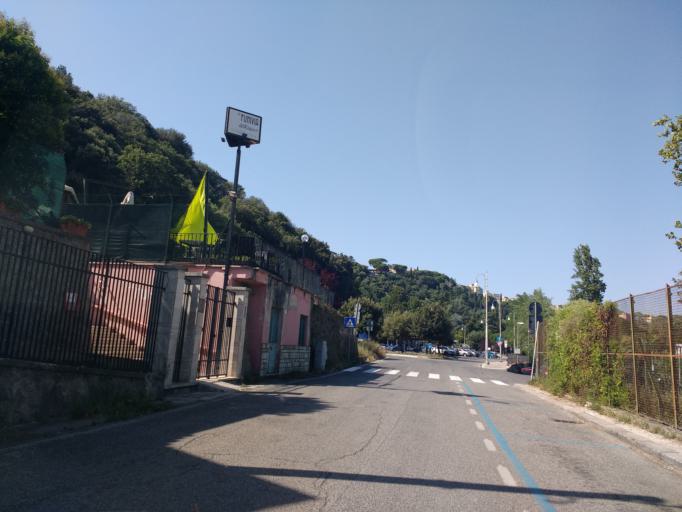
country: IT
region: Latium
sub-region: Citta metropolitana di Roma Capitale
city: Castel Gandolfo
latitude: 41.7538
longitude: 12.6509
